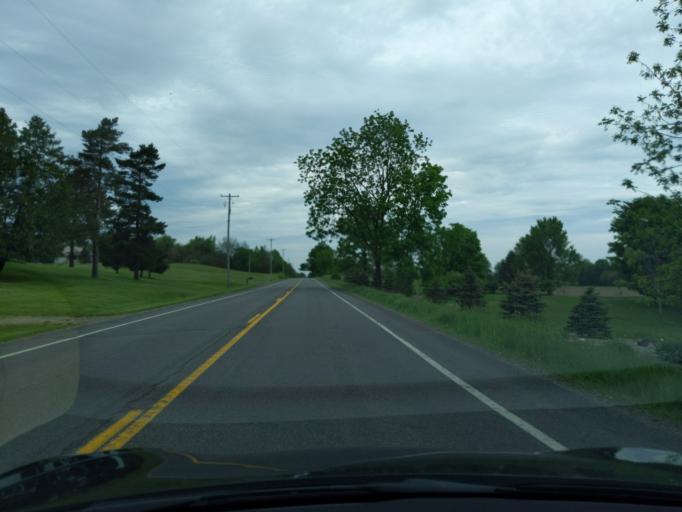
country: US
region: Michigan
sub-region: Ingham County
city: Mason
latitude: 42.5656
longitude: -84.3569
